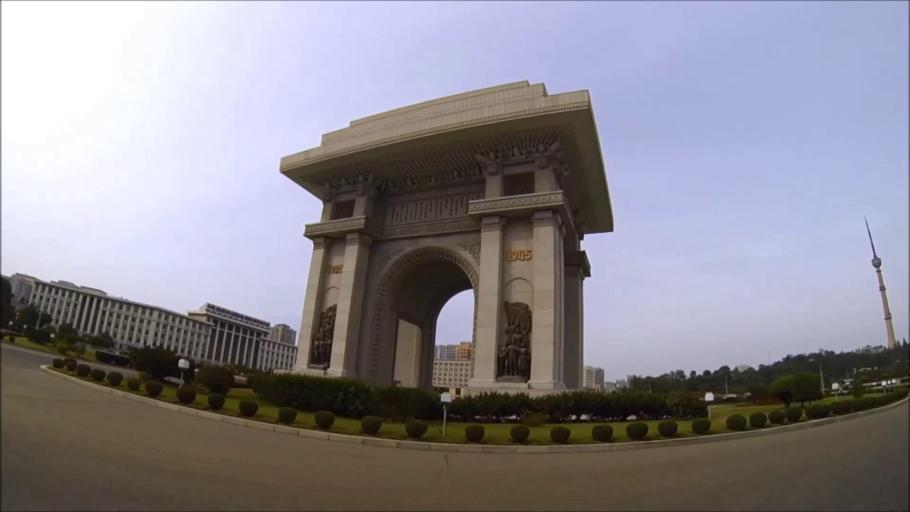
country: KP
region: Pyongyang
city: Pyongyang
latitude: 39.0437
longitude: 125.7531
